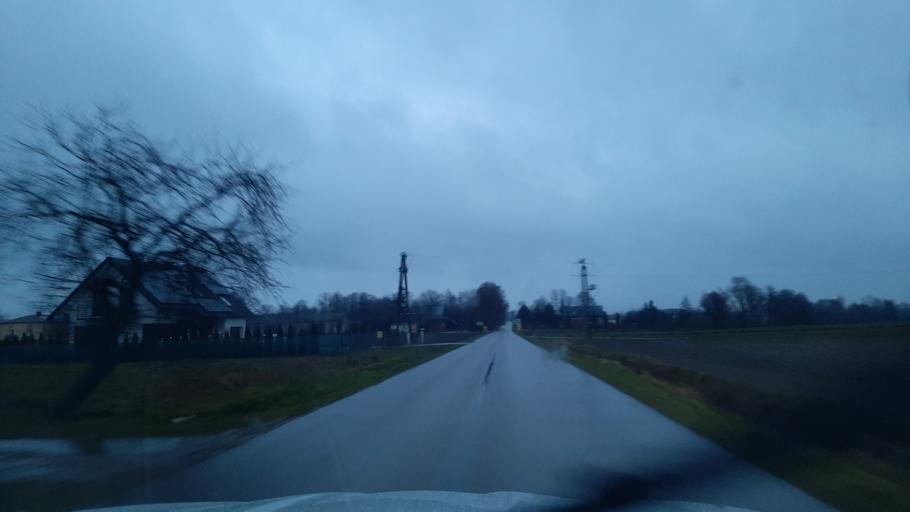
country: PL
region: Lublin Voivodeship
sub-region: Powiat lubelski
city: Jastkow
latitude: 51.3574
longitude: 22.4238
